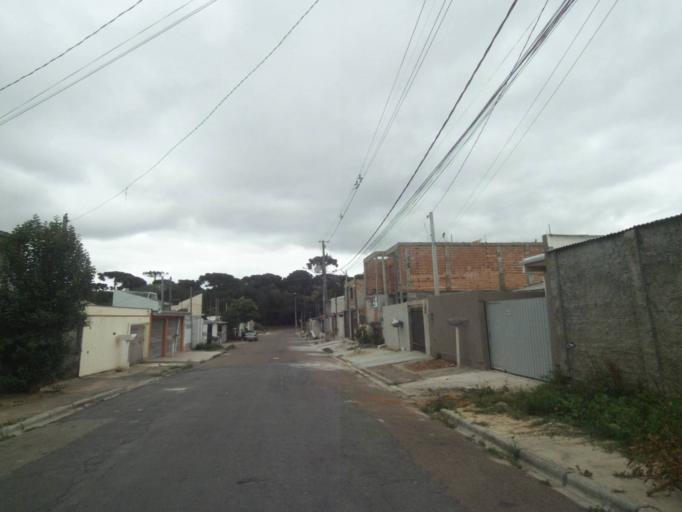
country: BR
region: Parana
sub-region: Sao Jose Dos Pinhais
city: Sao Jose dos Pinhais
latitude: -25.5577
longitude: -49.2623
